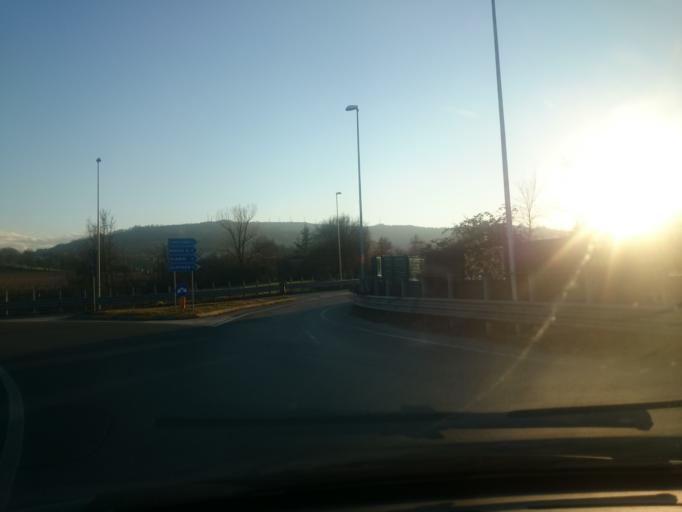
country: IT
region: Emilia-Romagna
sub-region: Provincia di Reggio Emilia
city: Scandiano
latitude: 44.5928
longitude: 10.7034
